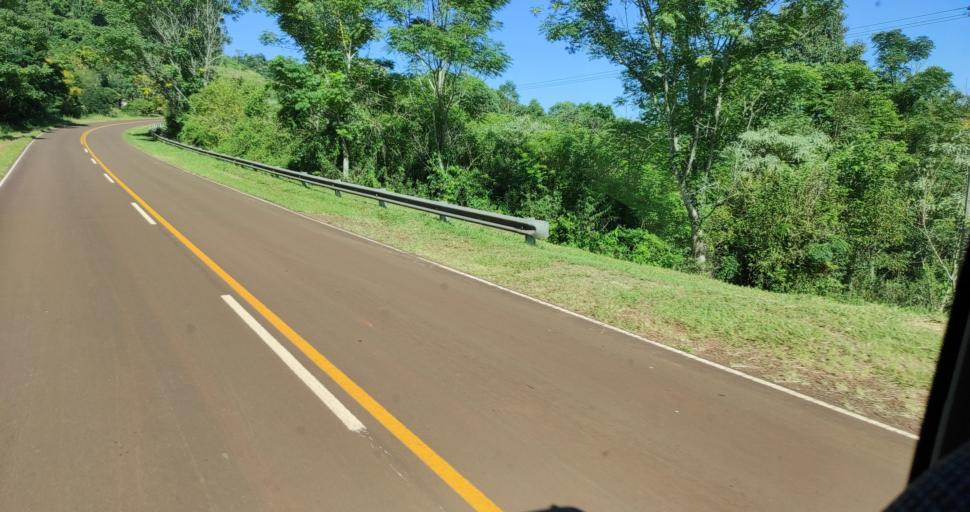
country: AR
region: Misiones
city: El Soberbio
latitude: -27.2252
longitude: -54.0583
